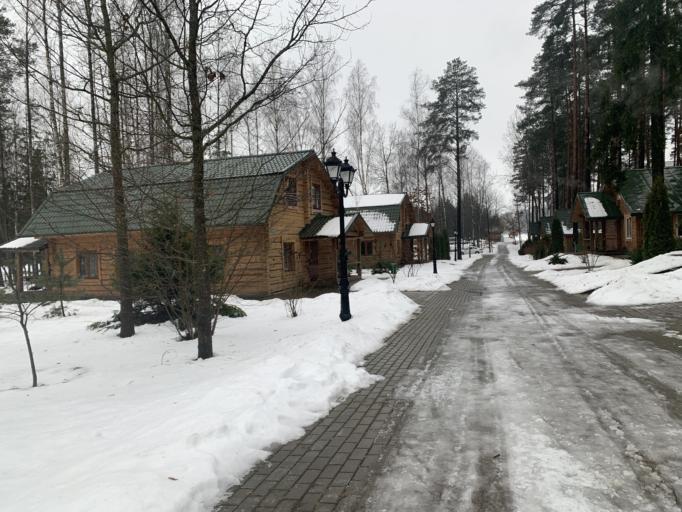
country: BY
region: Minsk
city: Slabada
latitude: 53.9479
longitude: 27.9838
